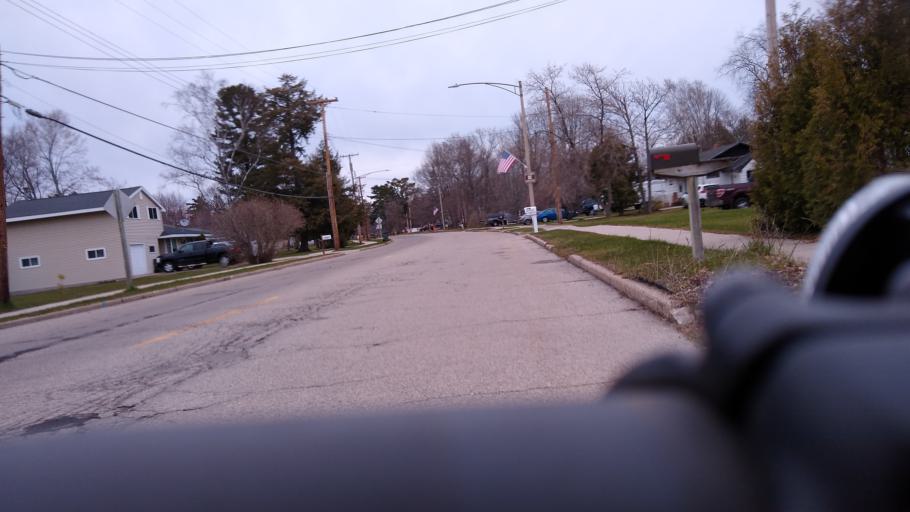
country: US
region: Michigan
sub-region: Delta County
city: Escanaba
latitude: 45.7155
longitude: -87.0794
